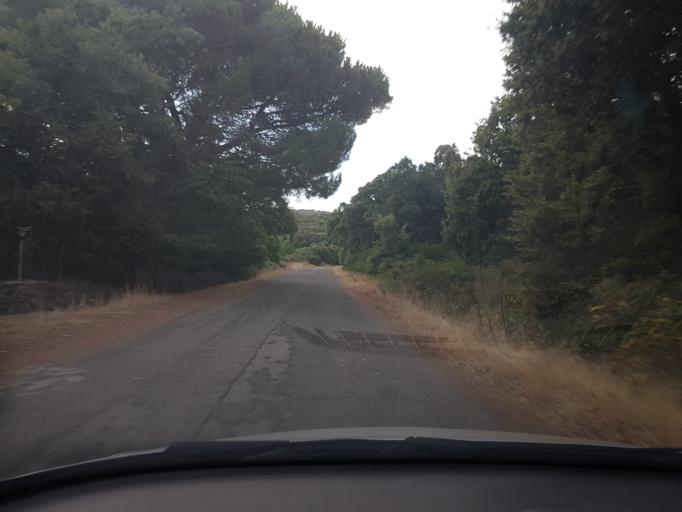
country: IT
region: Sardinia
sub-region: Provincia di Oristano
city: Seneghe
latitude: 40.1098
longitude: 8.6204
